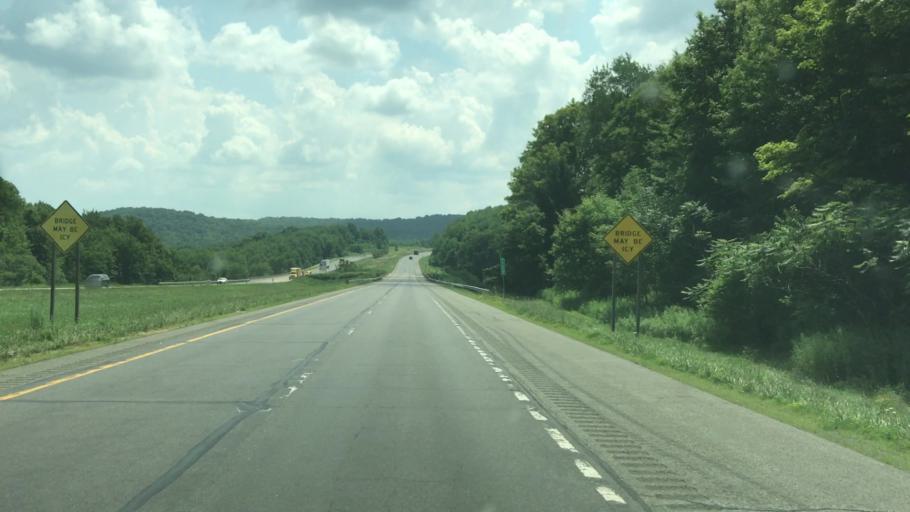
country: US
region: Pennsylvania
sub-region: Lackawanna County
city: Mount Cobb
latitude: 41.3675
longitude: -75.4416
